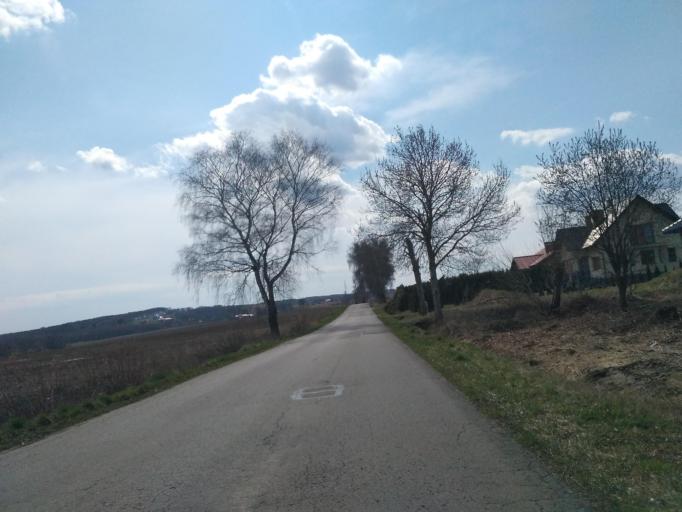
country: PL
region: Subcarpathian Voivodeship
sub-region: Powiat ropczycko-sedziszowski
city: Sedziszow Malopolski
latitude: 50.0590
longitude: 21.7145
